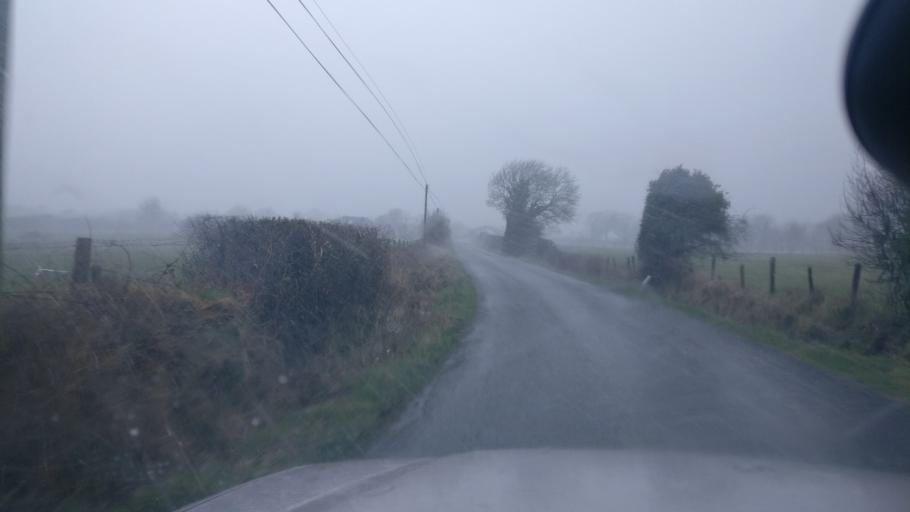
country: IE
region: Connaught
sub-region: County Galway
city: Loughrea
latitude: 53.2276
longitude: -8.3933
